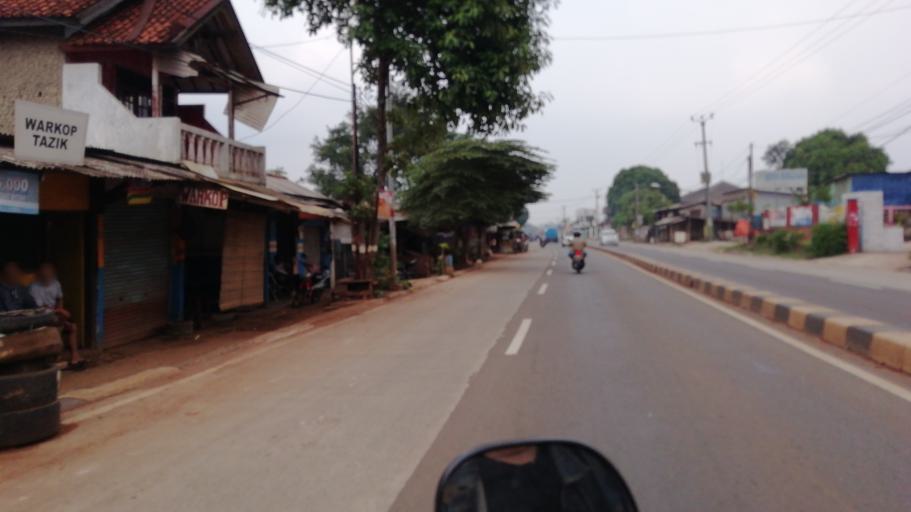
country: ID
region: West Java
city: Parung
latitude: -6.4619
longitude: 106.7300
